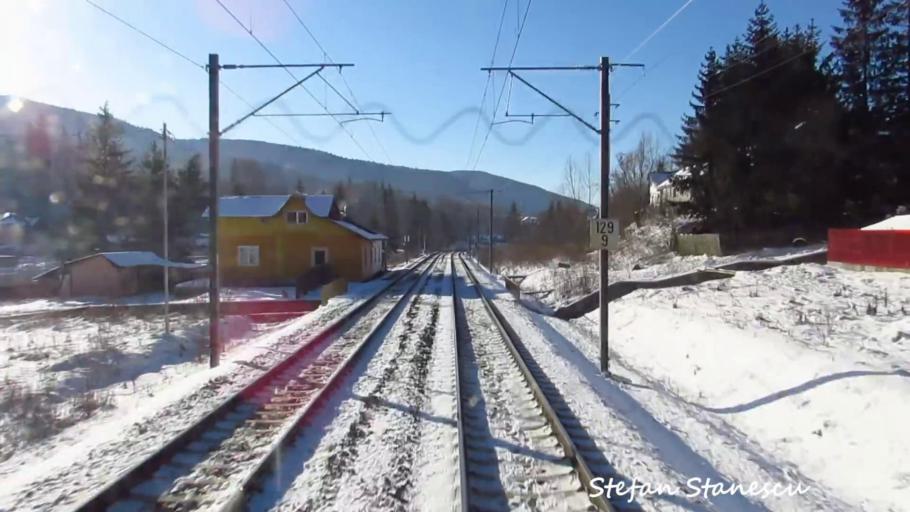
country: RO
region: Prahova
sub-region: Oras Busteni
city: Poiana Tapului
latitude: 45.3856
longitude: 25.5405
